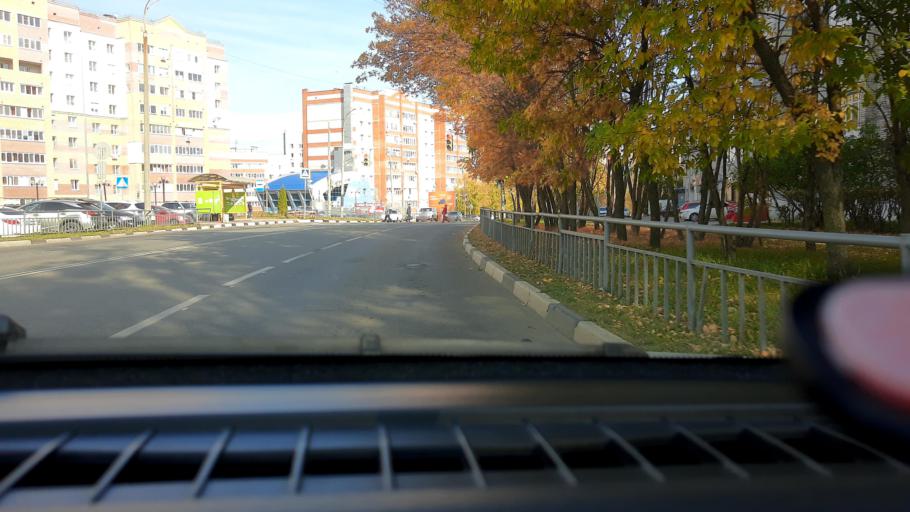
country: RU
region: Nizjnij Novgorod
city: Kstovo
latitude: 56.1458
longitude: 44.1786
